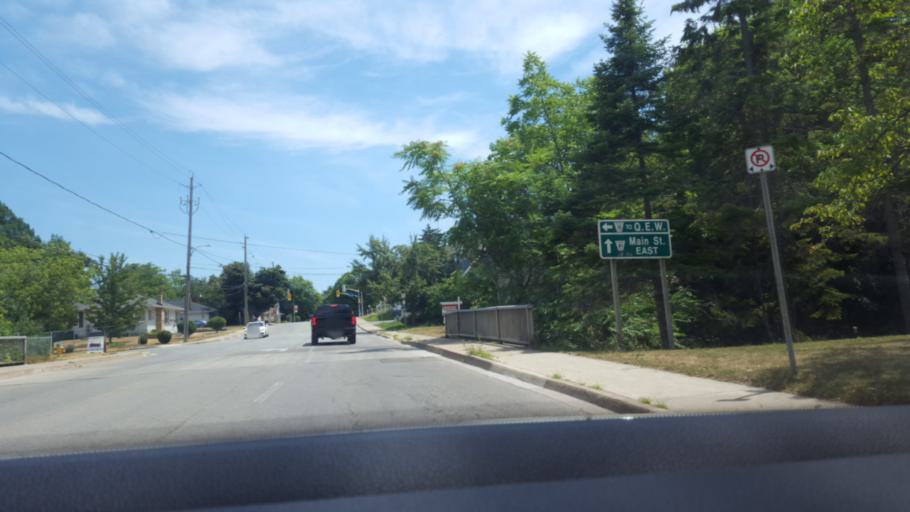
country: CA
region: Ontario
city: Oakville
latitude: 43.1928
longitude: -79.5648
